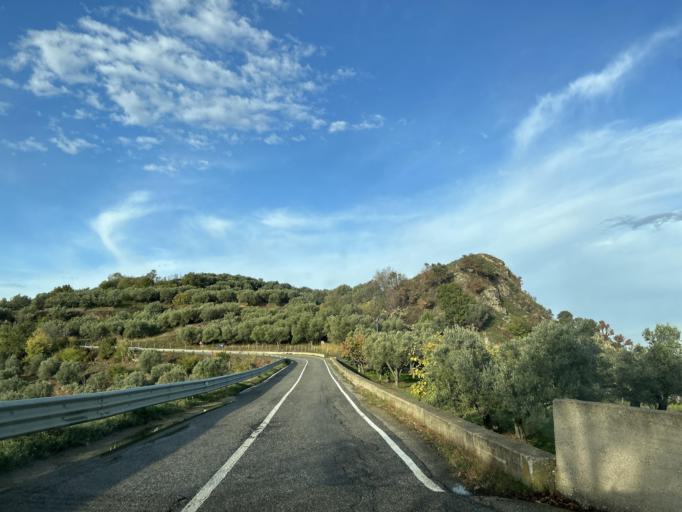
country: IT
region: Calabria
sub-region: Provincia di Catanzaro
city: Montauro
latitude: 38.7630
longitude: 16.5188
